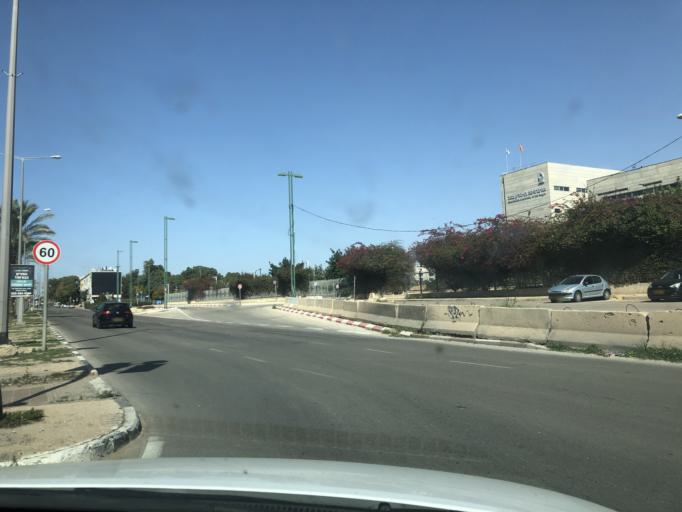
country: IL
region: Southern District
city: Beersheba
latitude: 31.2621
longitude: 34.7982
